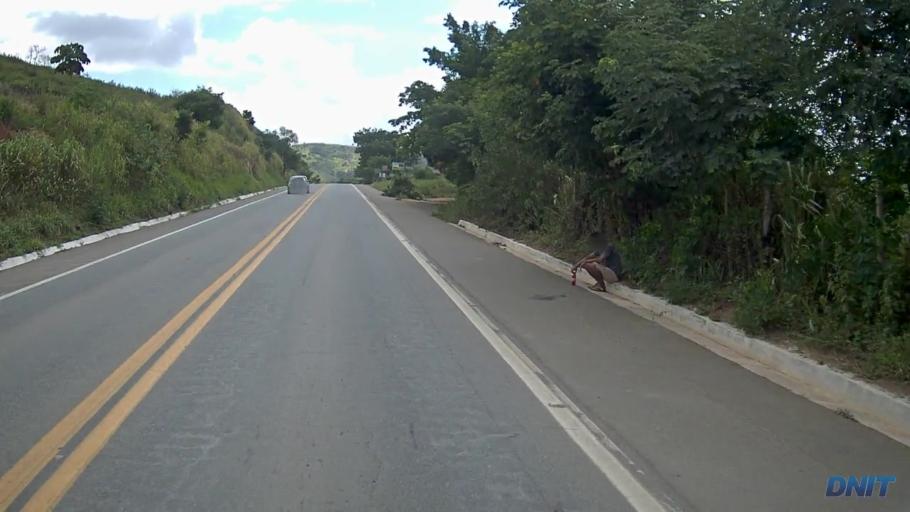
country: BR
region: Minas Gerais
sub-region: Governador Valadares
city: Governador Valadares
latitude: -18.9282
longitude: -42.0417
